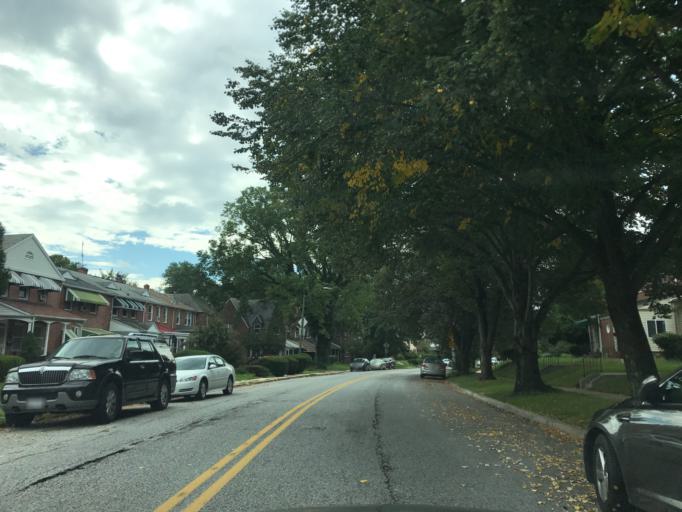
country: US
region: Maryland
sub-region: Baltimore County
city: Lochearn
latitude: 39.3268
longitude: -76.6650
